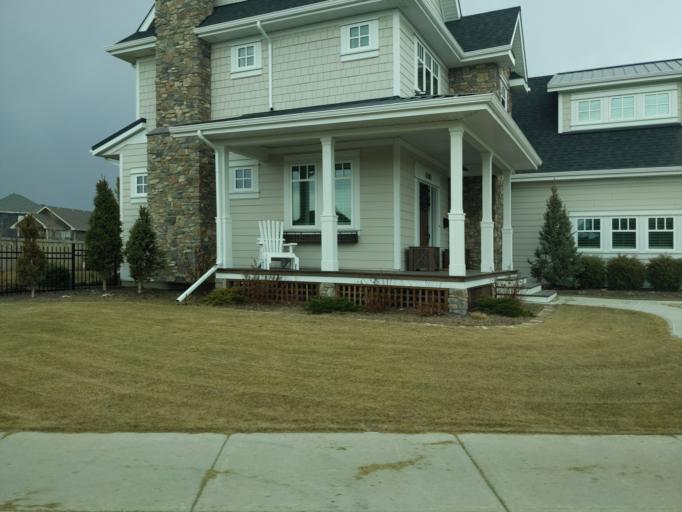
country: CA
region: Saskatchewan
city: Lloydminster
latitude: 53.2557
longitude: -110.0398
